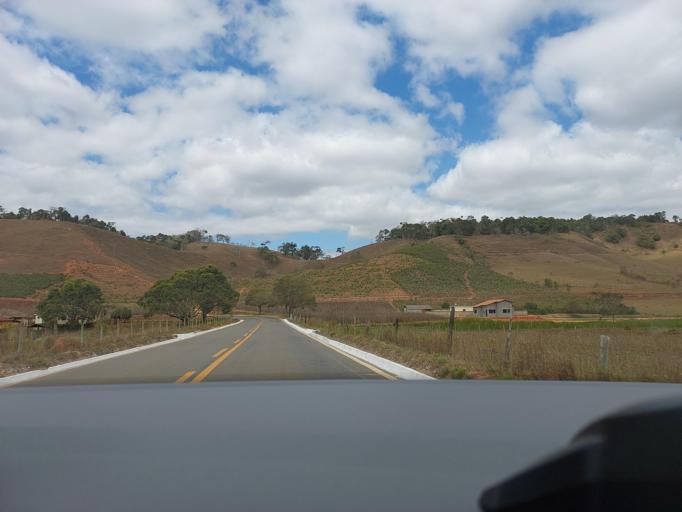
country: BR
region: Minas Gerais
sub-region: Vicosa
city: Vicosa
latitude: -20.8504
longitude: -42.6748
